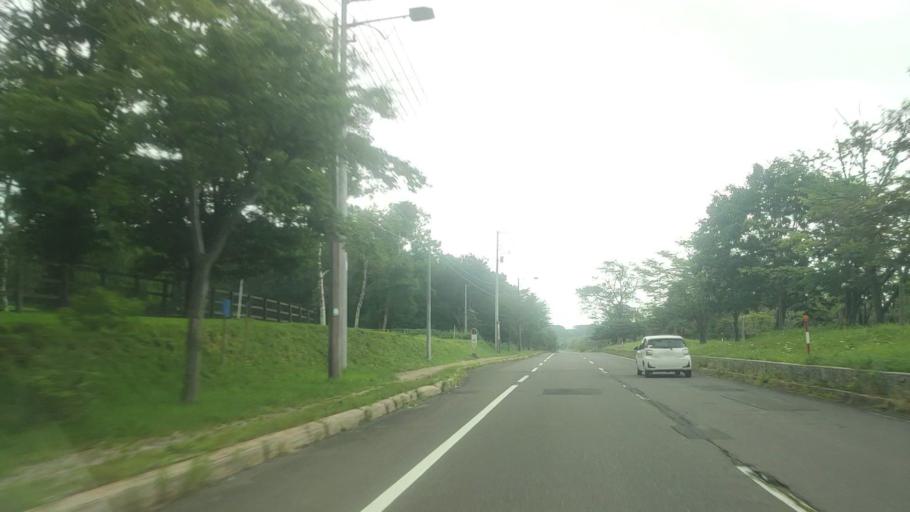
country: JP
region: Hokkaido
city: Shiraoi
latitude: 42.4689
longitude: 141.1612
